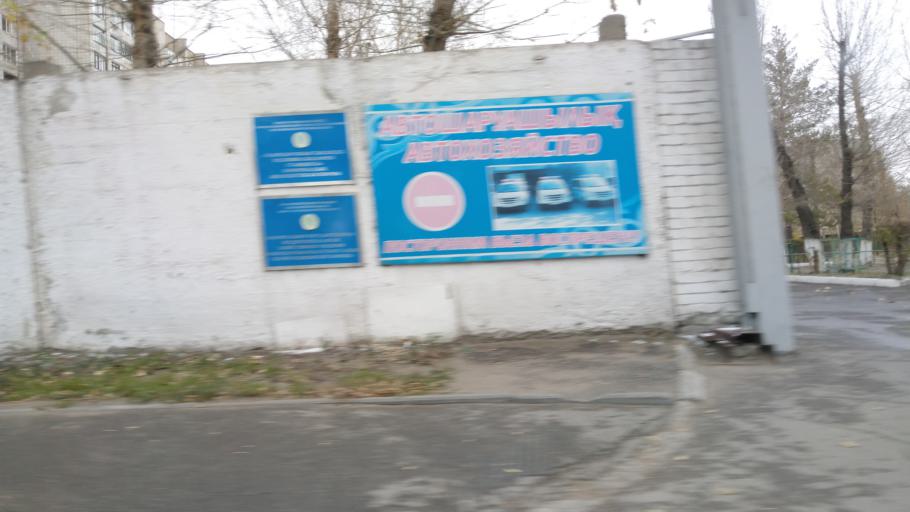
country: KZ
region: Pavlodar
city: Pavlodar
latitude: 52.2761
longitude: 76.9621
